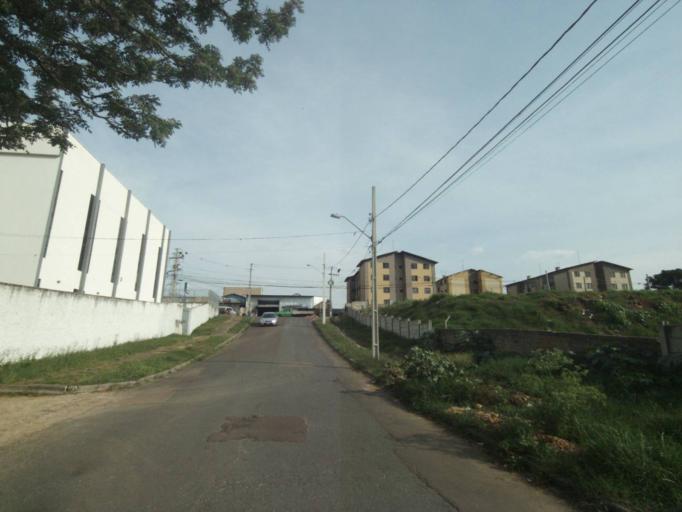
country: BR
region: Parana
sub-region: Curitiba
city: Curitiba
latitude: -25.4643
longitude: -49.3153
